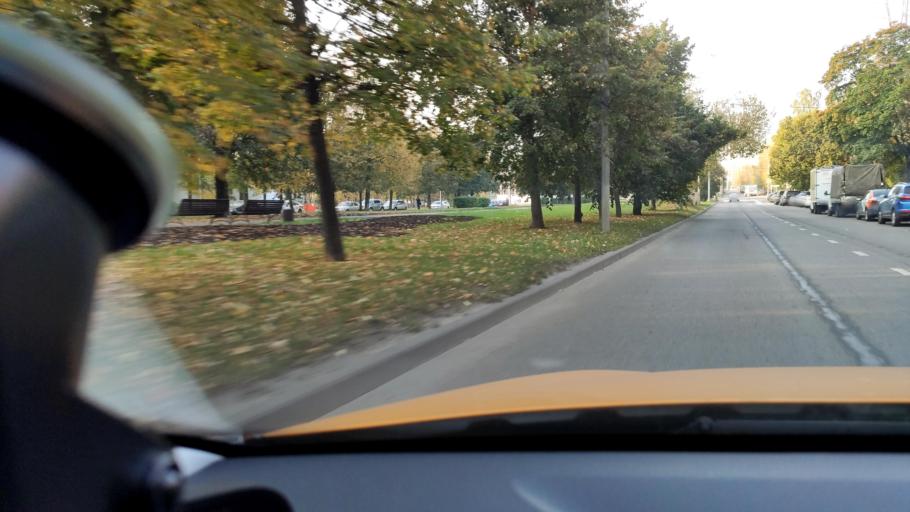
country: RU
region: Moscow
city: Metrogorodok
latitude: 55.8231
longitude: 37.7642
